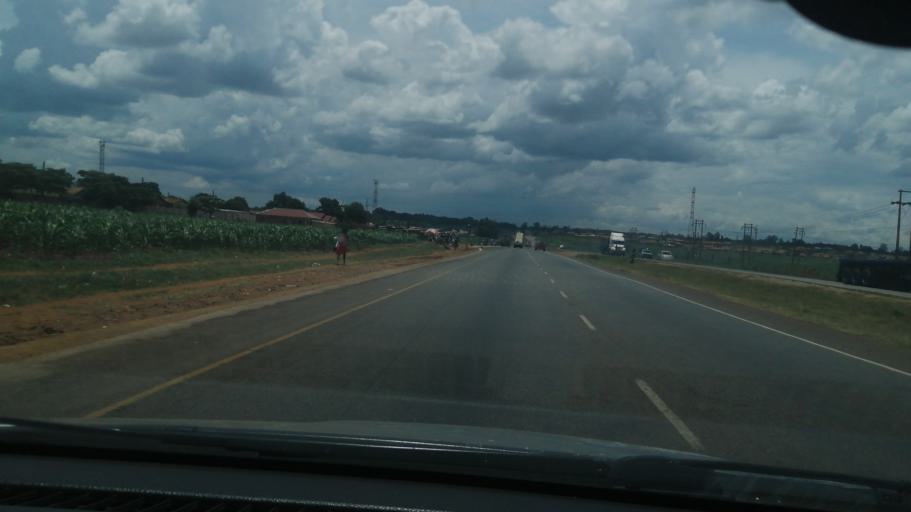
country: ZW
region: Harare
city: Harare
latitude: -17.8194
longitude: 30.9154
